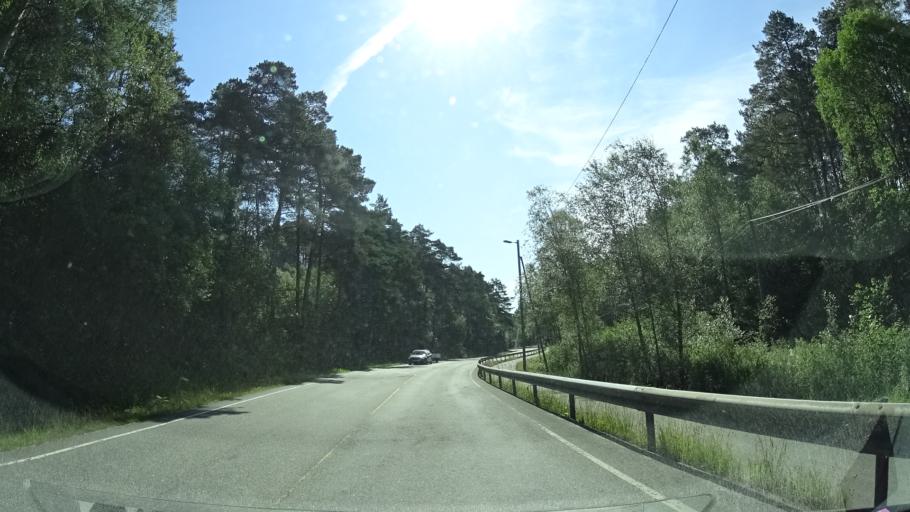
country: NO
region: Hordaland
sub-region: Stord
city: Sagvag
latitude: 59.7719
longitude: 5.4057
